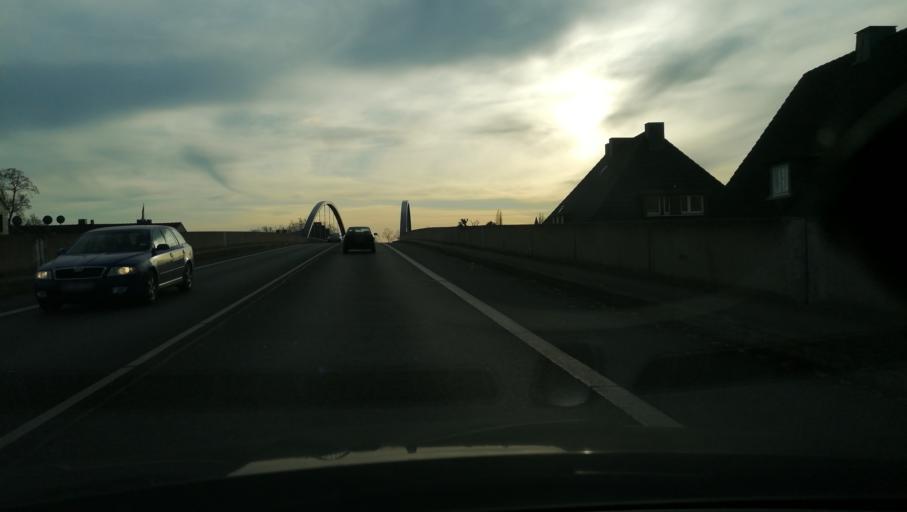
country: DE
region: North Rhine-Westphalia
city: Waltrop
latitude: 51.5713
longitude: 7.3771
